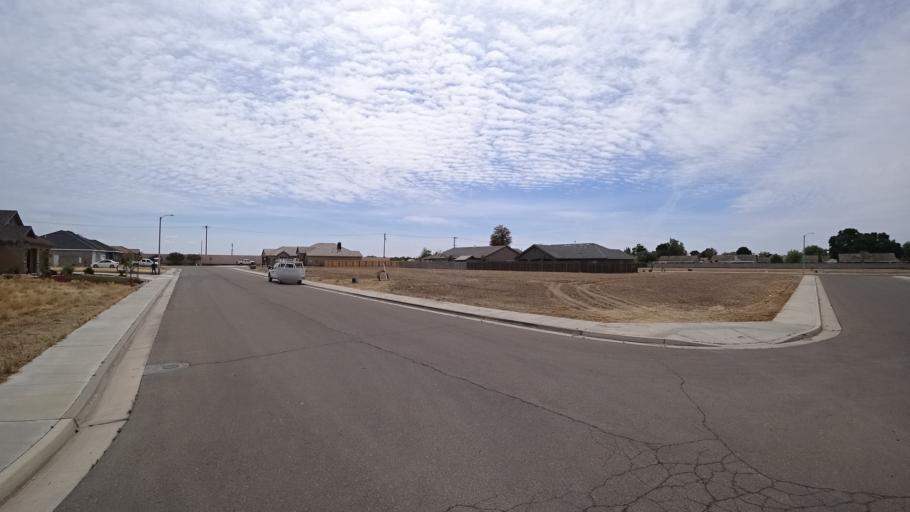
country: US
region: California
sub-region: Kings County
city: Lucerne
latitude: 36.3701
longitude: -119.6387
